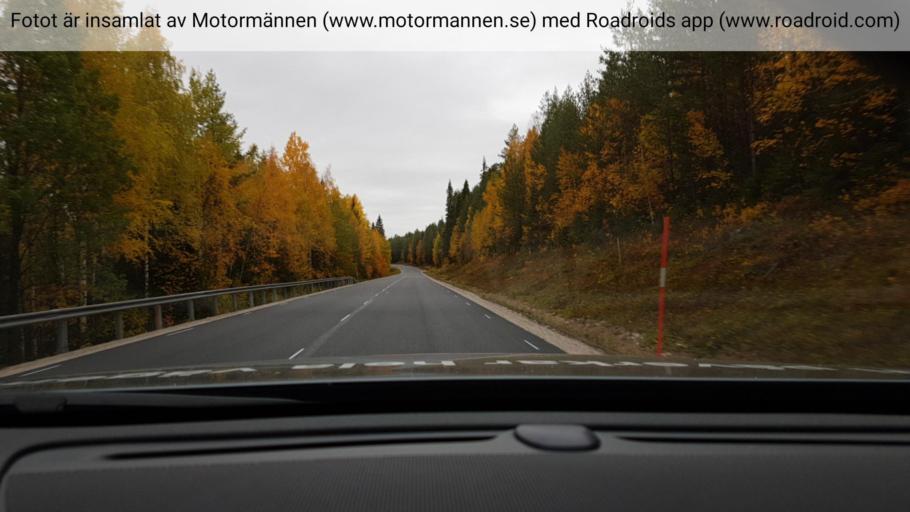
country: SE
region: Norrbotten
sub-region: Overkalix Kommun
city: OEverkalix
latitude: 66.4656
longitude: 22.7928
